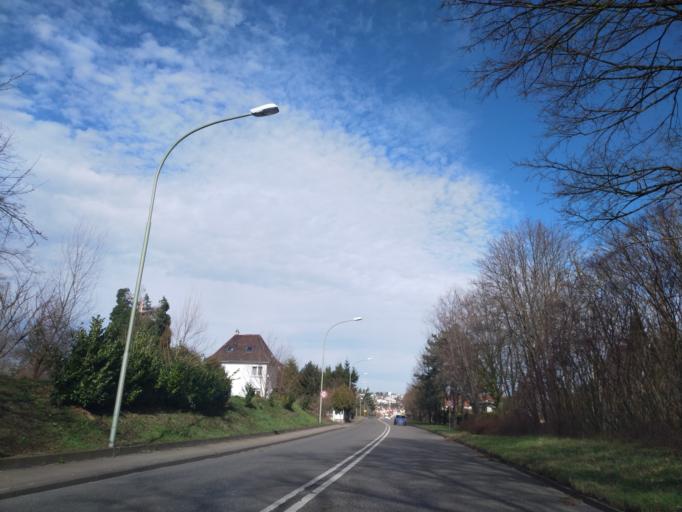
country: DE
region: Baden-Wuerttemberg
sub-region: Karlsruhe Region
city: Birkenfeld
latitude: 48.8764
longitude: 8.6652
